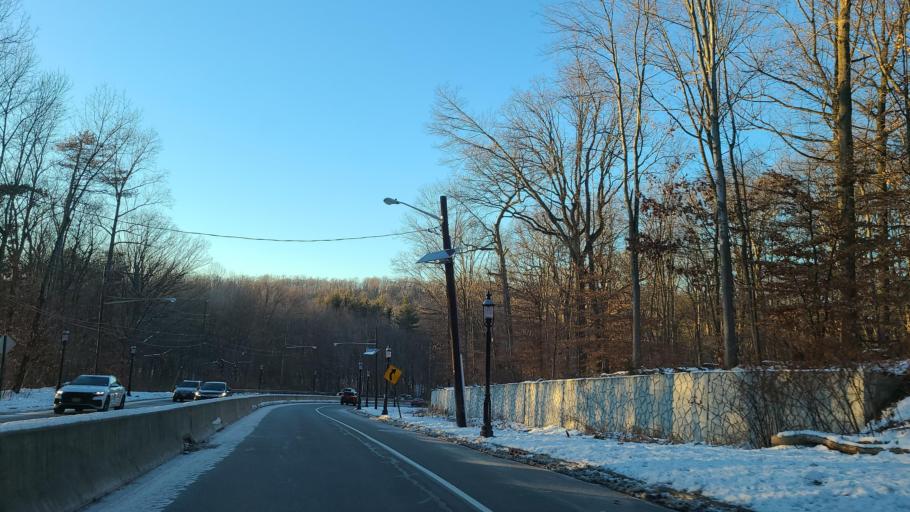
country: US
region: New Jersey
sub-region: Essex County
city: Maplewood
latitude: 40.7519
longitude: -74.2881
